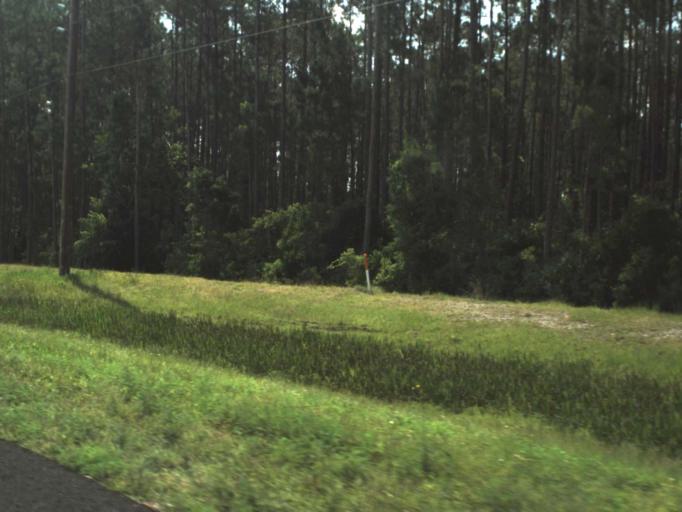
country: US
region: Florida
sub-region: Volusia County
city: Samsula-Spruce Creek
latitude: 29.0118
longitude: -81.0292
